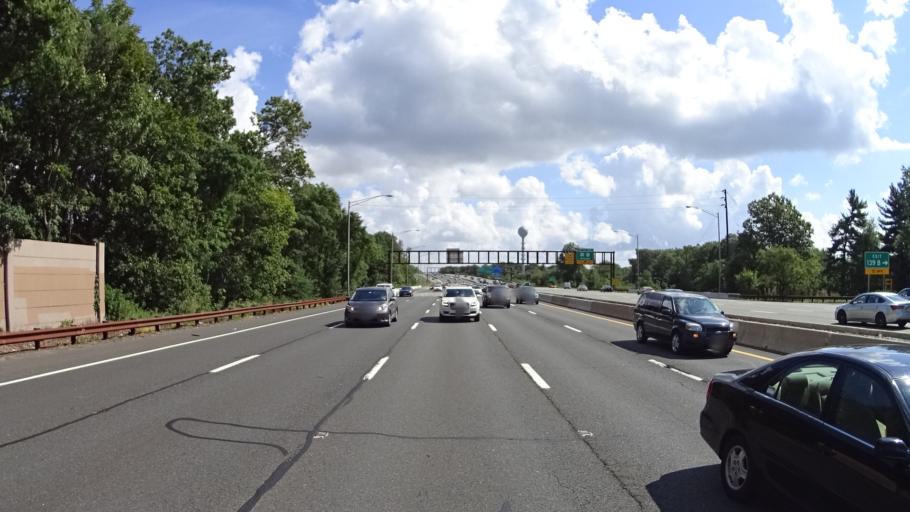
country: US
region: New Jersey
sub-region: Union County
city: Union
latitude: 40.6909
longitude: -74.2685
